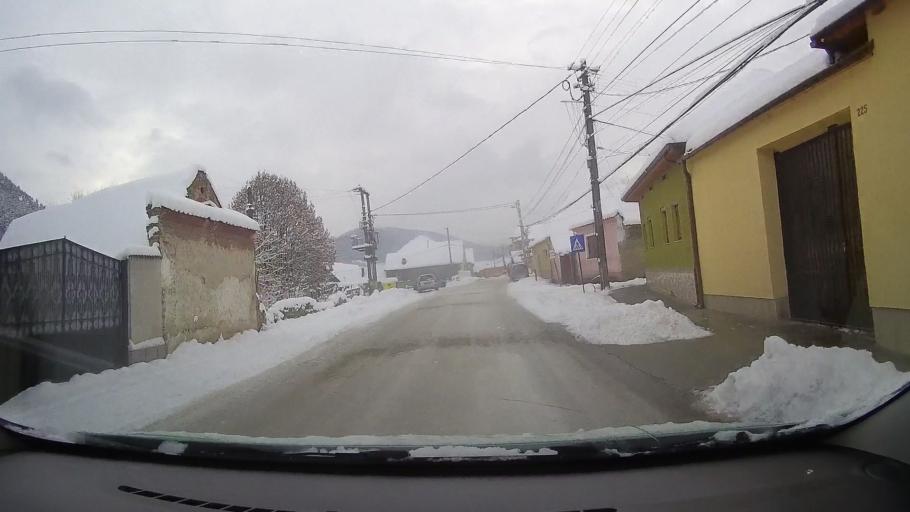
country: RO
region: Alba
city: Pianu de Sus
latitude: 45.8966
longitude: 23.4819
